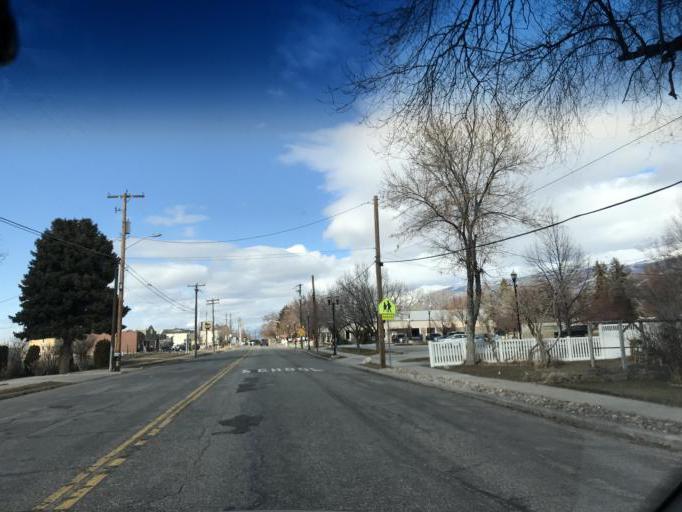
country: US
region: Utah
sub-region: Davis County
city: Woods Cross
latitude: 40.8731
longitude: -111.9021
